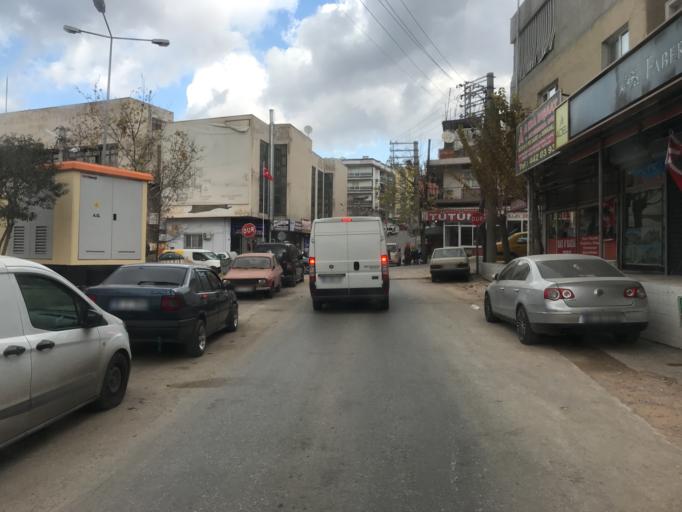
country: TR
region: Izmir
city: Buca
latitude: 38.4026
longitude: 27.1663
